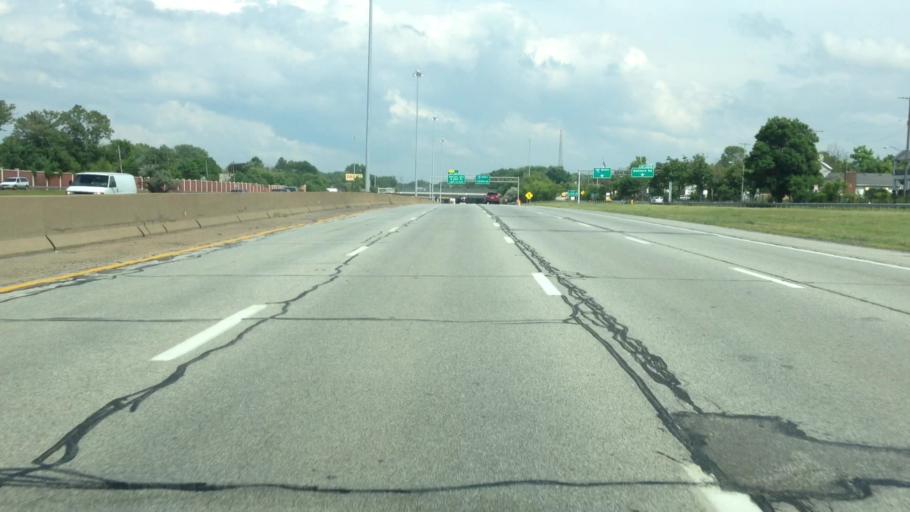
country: US
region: Ohio
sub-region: Cuyahoga County
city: Brooklyn
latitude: 41.4453
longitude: -81.7753
